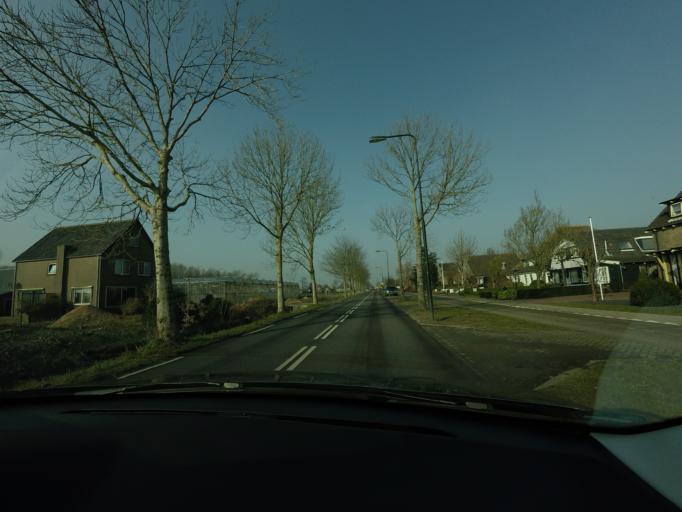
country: NL
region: North Holland
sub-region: Gemeente Heerhugowaard
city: Heerhugowaard
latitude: 52.6493
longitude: 4.8479
